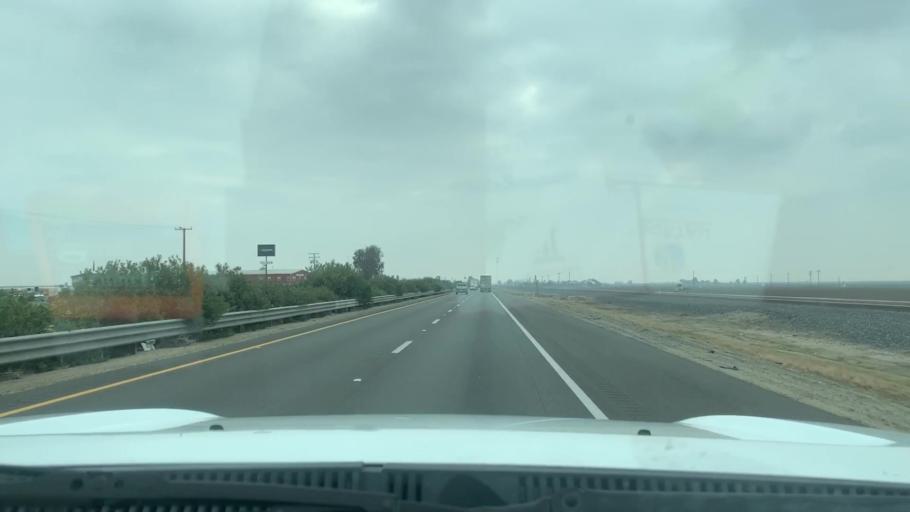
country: US
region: California
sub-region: Tulare County
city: Tipton
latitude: 36.0855
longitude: -119.3204
